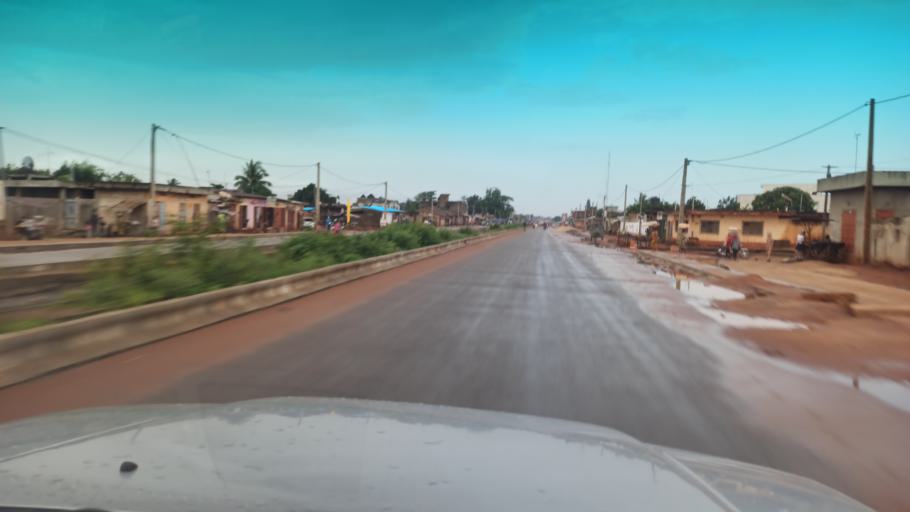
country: BJ
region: Queme
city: Porto-Novo
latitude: 6.4978
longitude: 2.6264
